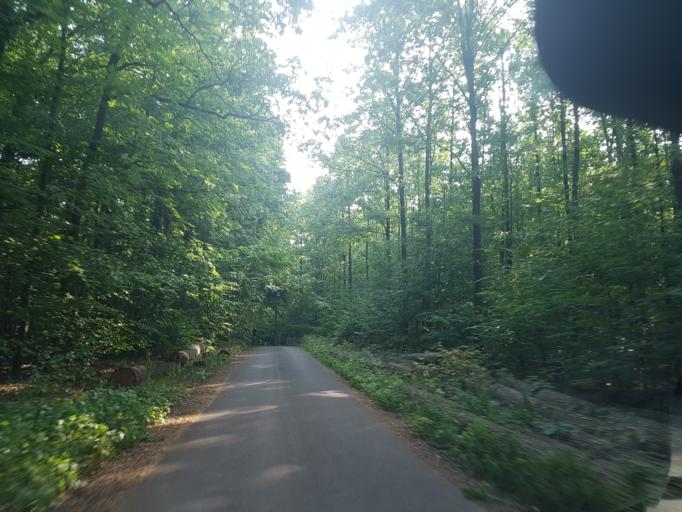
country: DE
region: Brandenburg
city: Wiesenburg
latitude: 52.0407
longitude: 12.3750
